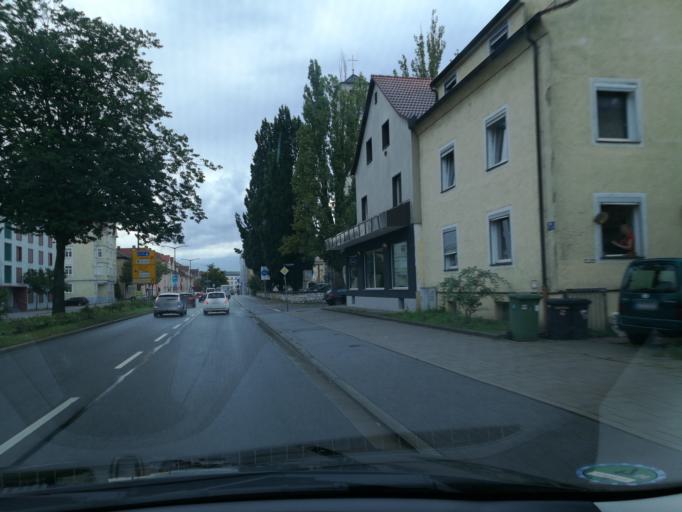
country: DE
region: Bavaria
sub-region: Upper Palatinate
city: Regensburg
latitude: 49.0094
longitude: 12.1081
